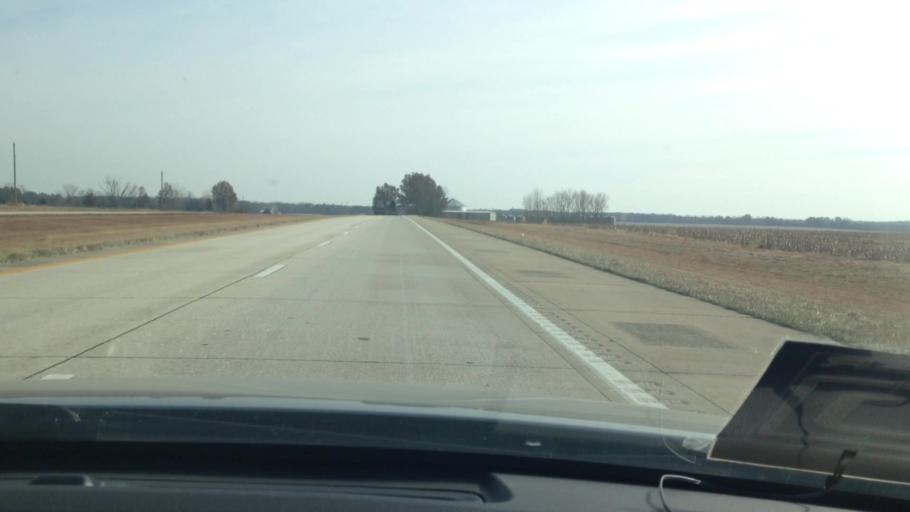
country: US
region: Missouri
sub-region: Henry County
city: Clinton
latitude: 38.4311
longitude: -93.9265
